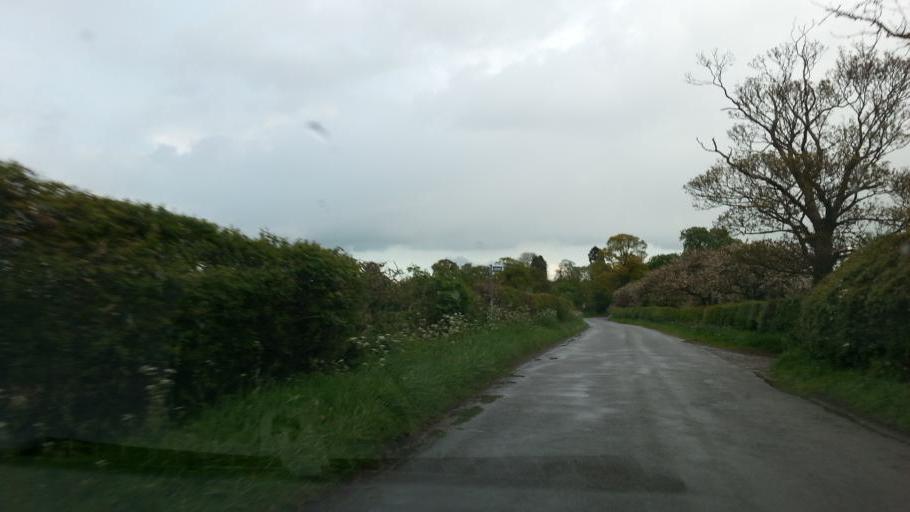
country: GB
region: England
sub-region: Nottinghamshire
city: Farndon
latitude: 52.9911
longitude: -0.8443
